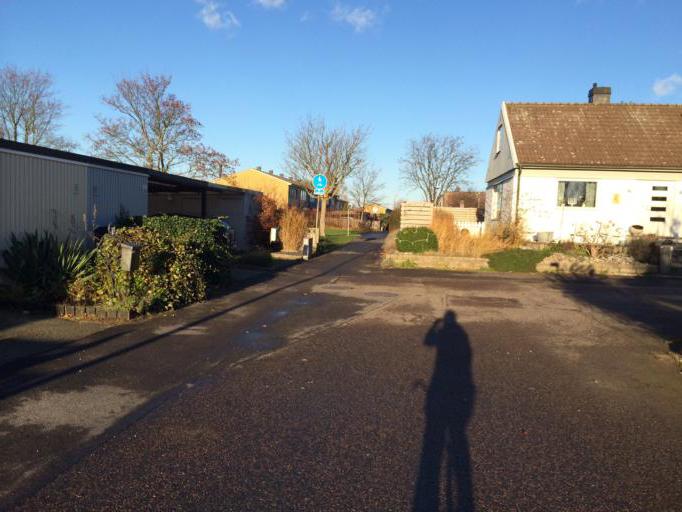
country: SE
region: Skane
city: Bjarred
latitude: 55.7272
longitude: 13.0174
